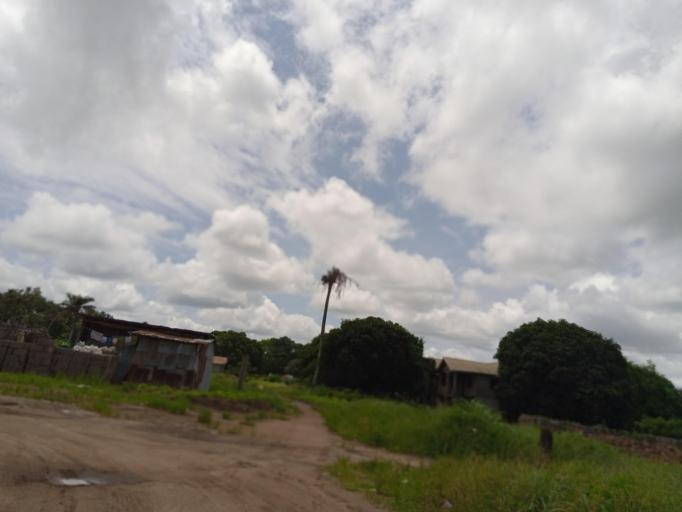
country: SL
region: Northern Province
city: Masoyila
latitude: 8.5967
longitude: -13.1872
